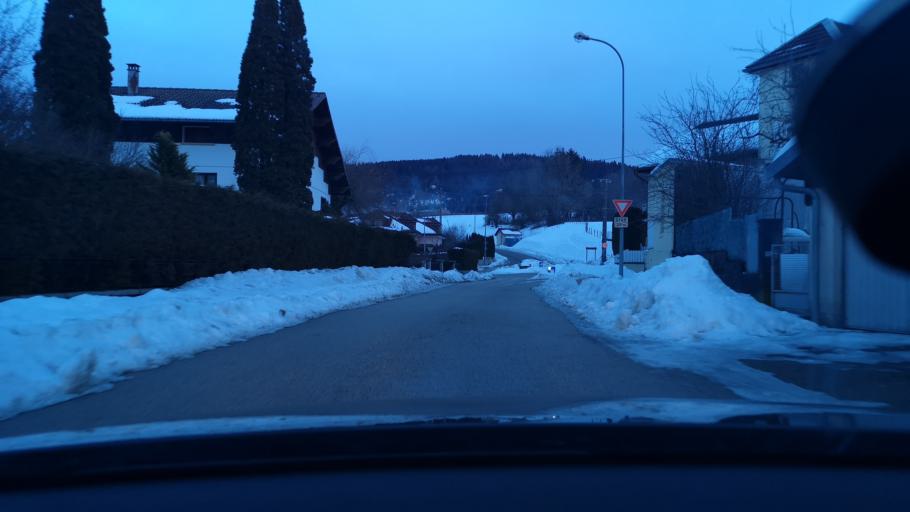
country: FR
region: Franche-Comte
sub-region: Departement du Doubs
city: Pontarlier
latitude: 46.9041
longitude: 6.3656
